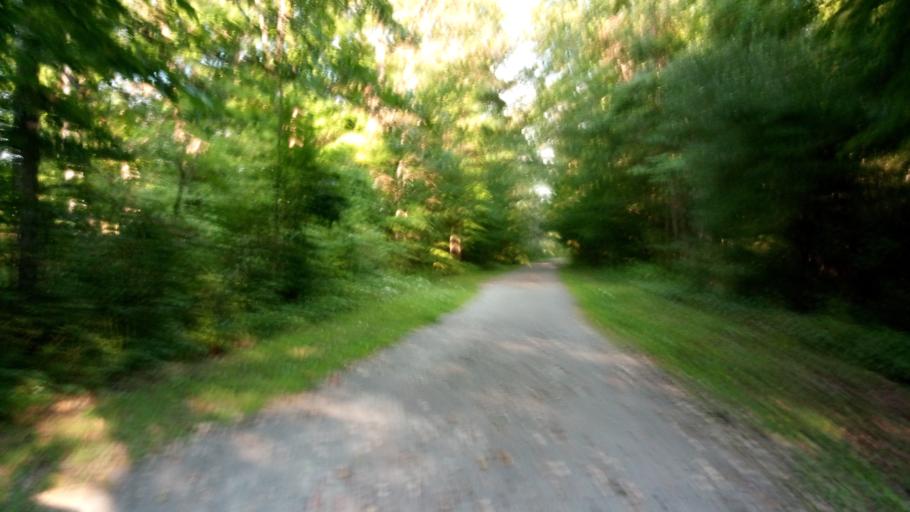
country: US
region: New York
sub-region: Ontario County
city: Victor
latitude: 42.9995
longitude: -77.4417
